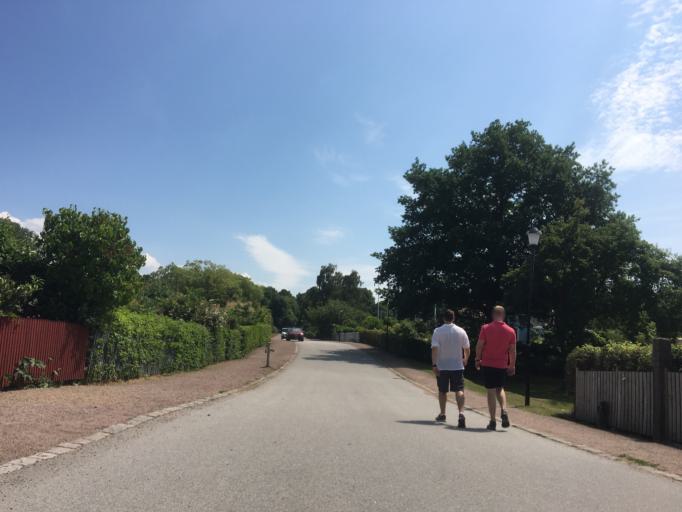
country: SE
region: Skane
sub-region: Landskrona
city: Landskrona
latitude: 55.8750
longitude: 12.8266
